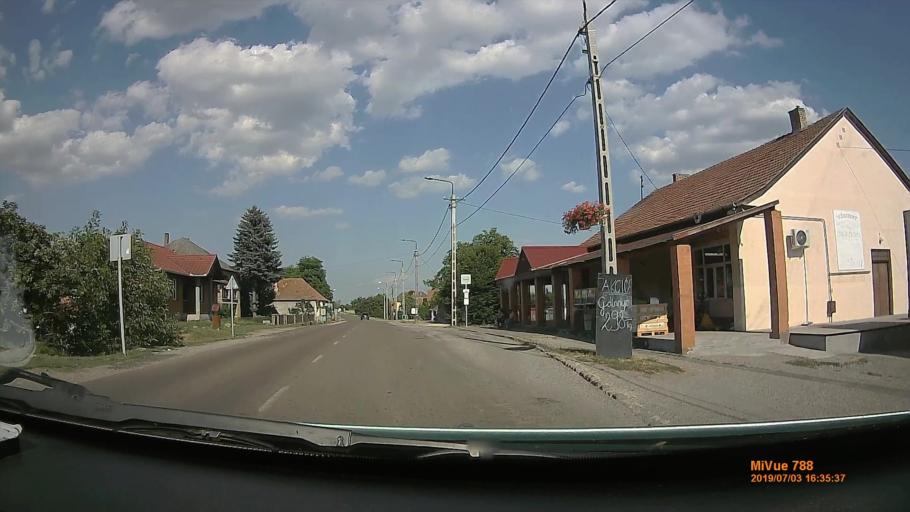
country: HU
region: Borsod-Abauj-Zemplen
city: Sajokaza
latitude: 48.2738
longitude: 20.5567
